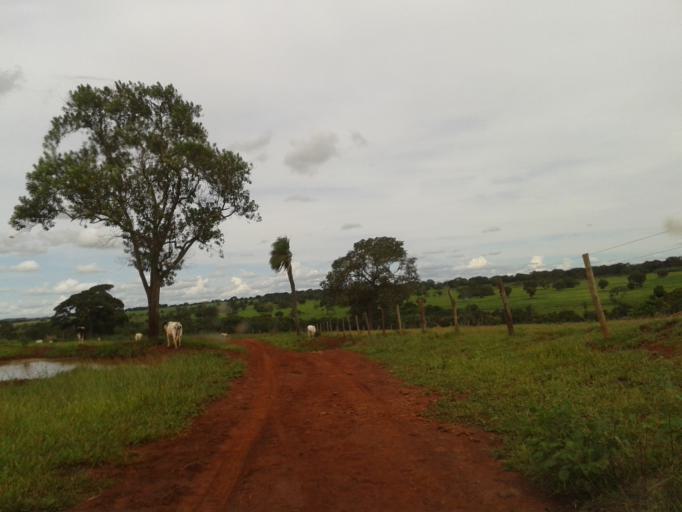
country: BR
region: Minas Gerais
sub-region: Santa Vitoria
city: Santa Vitoria
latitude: -18.7940
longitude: -49.8448
